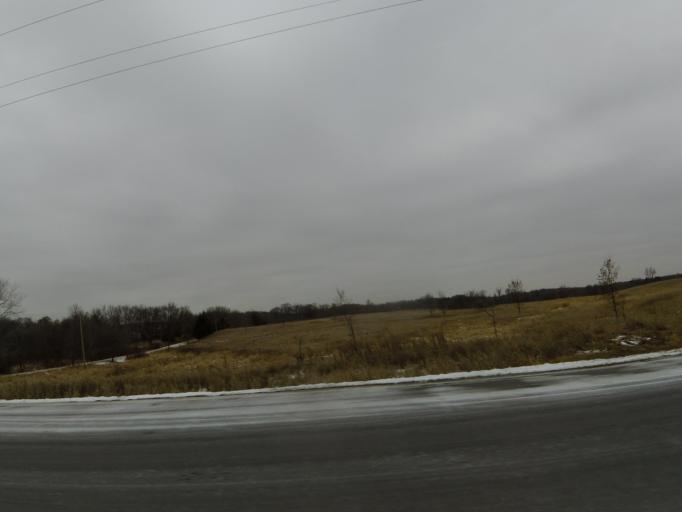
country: US
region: Minnesota
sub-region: Hennepin County
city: Medina
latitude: 45.0224
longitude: -93.6049
